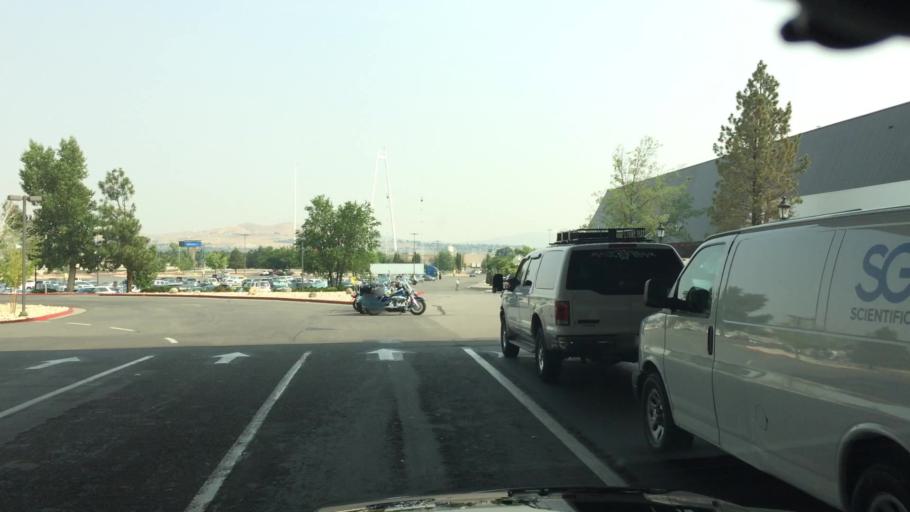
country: US
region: Nevada
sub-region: Washoe County
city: Sparks
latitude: 39.5235
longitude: -119.7810
